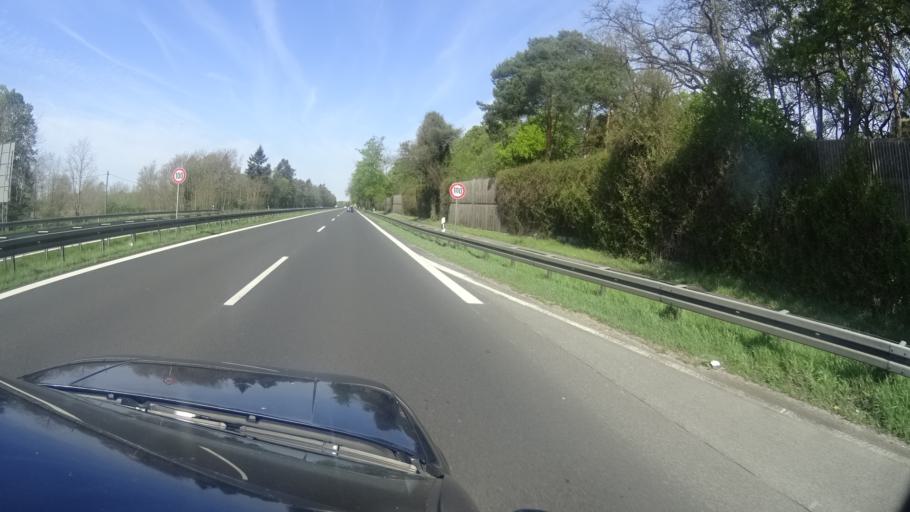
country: DE
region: Brandenburg
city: Wustermark
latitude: 52.5353
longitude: 12.9937
